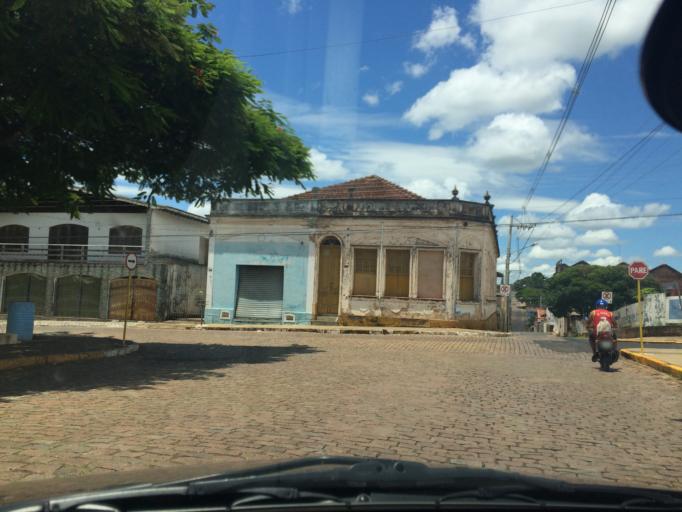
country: BR
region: Sao Paulo
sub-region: Casa Branca
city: Casa Branca
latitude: -21.7720
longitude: -47.0869
